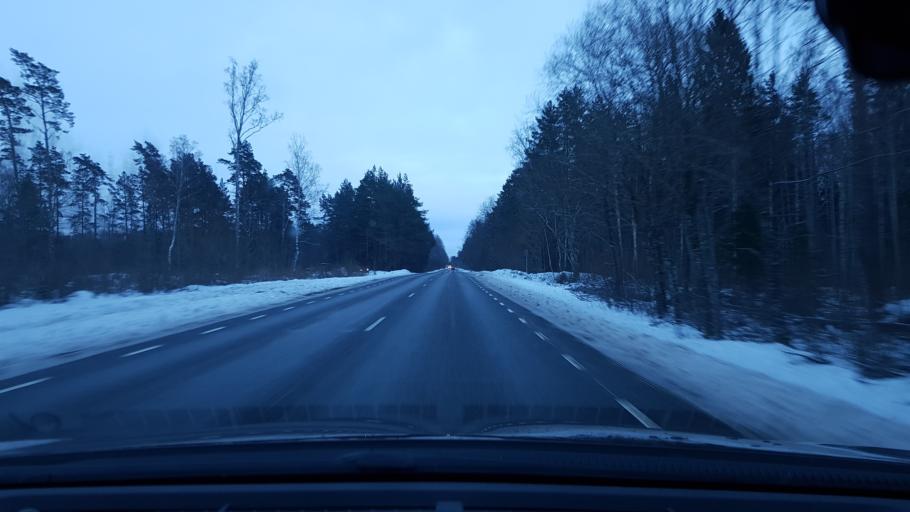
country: EE
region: Laeaene
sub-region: Ridala Parish
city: Uuemoisa
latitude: 59.0016
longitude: 23.6994
